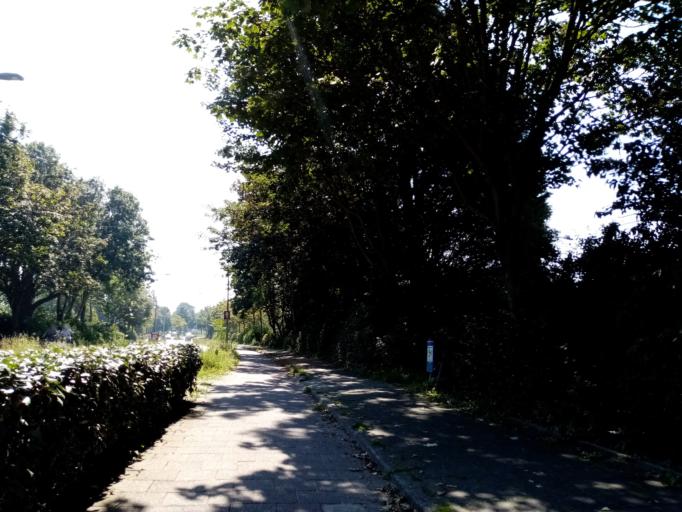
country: NL
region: South Holland
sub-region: Gemeente Lisse
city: Lisse
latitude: 52.2540
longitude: 4.5593
